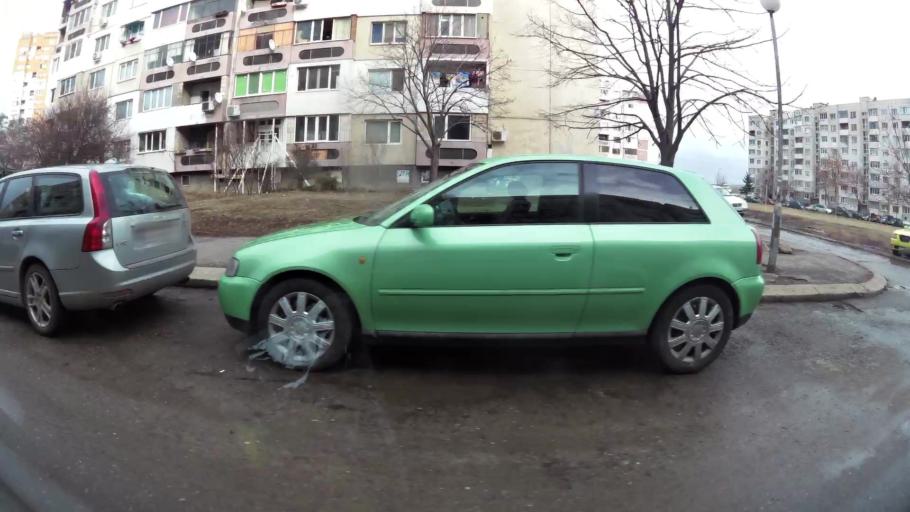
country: BG
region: Sofia-Capital
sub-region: Stolichna Obshtina
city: Sofia
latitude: 42.7464
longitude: 23.2782
